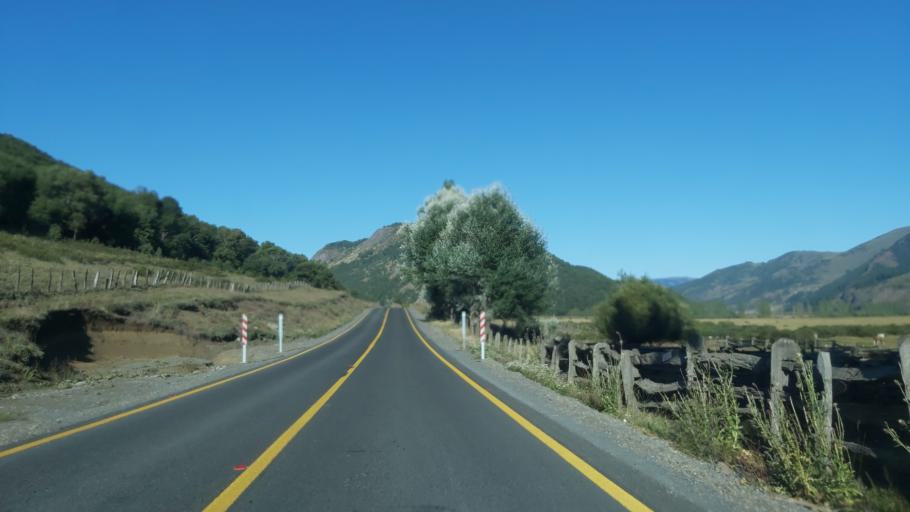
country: AR
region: Neuquen
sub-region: Departamento de Loncopue
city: Loncopue
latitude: -38.4456
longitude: -71.3526
